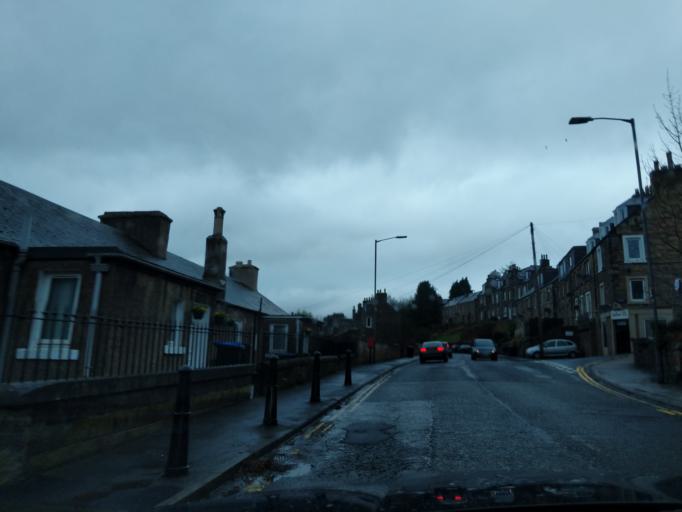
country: GB
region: Scotland
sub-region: The Scottish Borders
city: Galashiels
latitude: 55.6228
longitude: -2.8171
